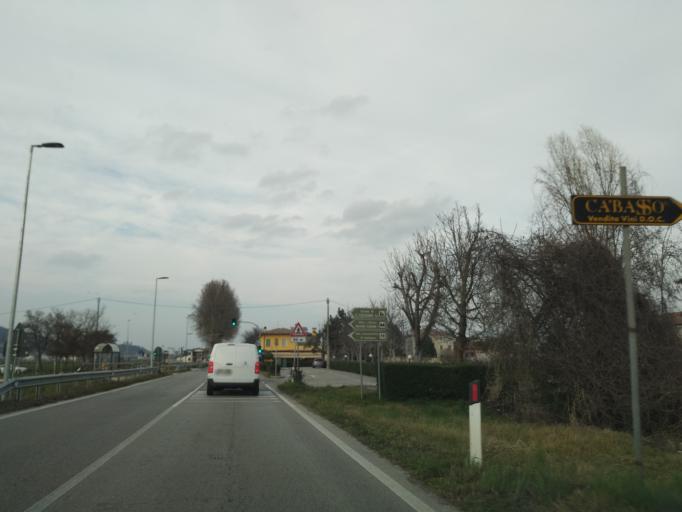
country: IT
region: Veneto
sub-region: Provincia di Vicenza
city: Lumignano
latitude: 45.4532
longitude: 11.6022
